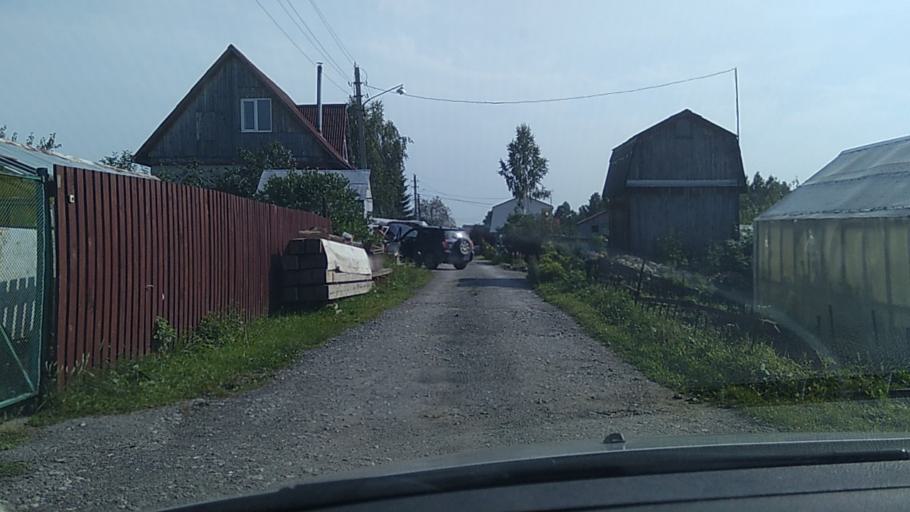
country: RU
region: Sverdlovsk
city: Sredneuralsk
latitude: 56.9696
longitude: 60.4676
